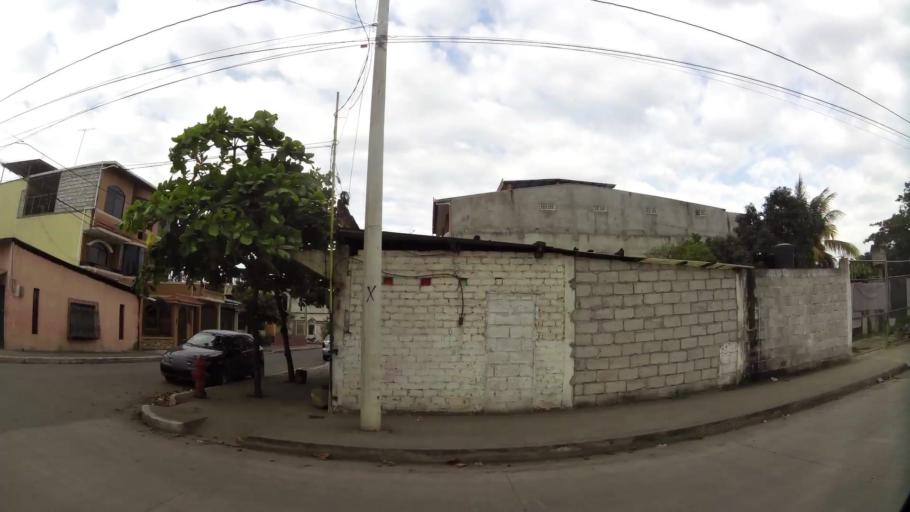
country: EC
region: El Oro
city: Machala
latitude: -3.2656
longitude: -79.9456
